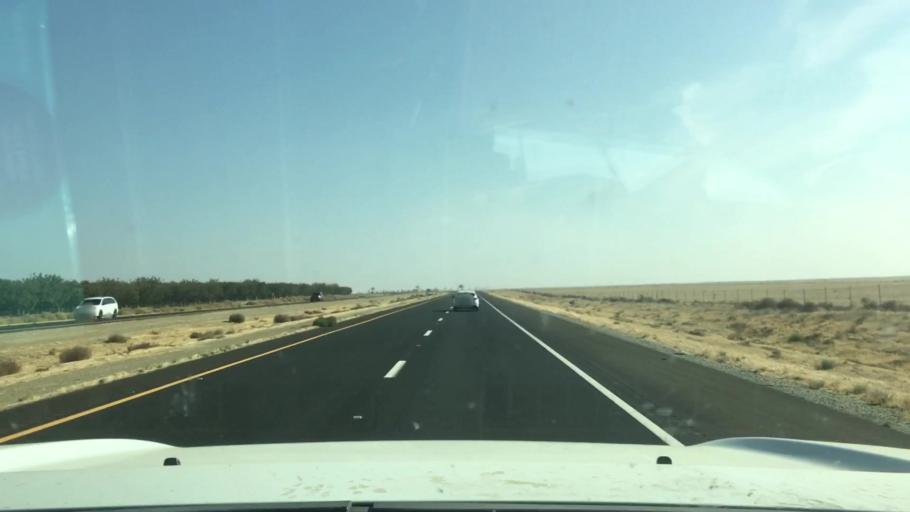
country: US
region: California
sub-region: Kern County
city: Lost Hills
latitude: 35.6170
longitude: -119.9701
